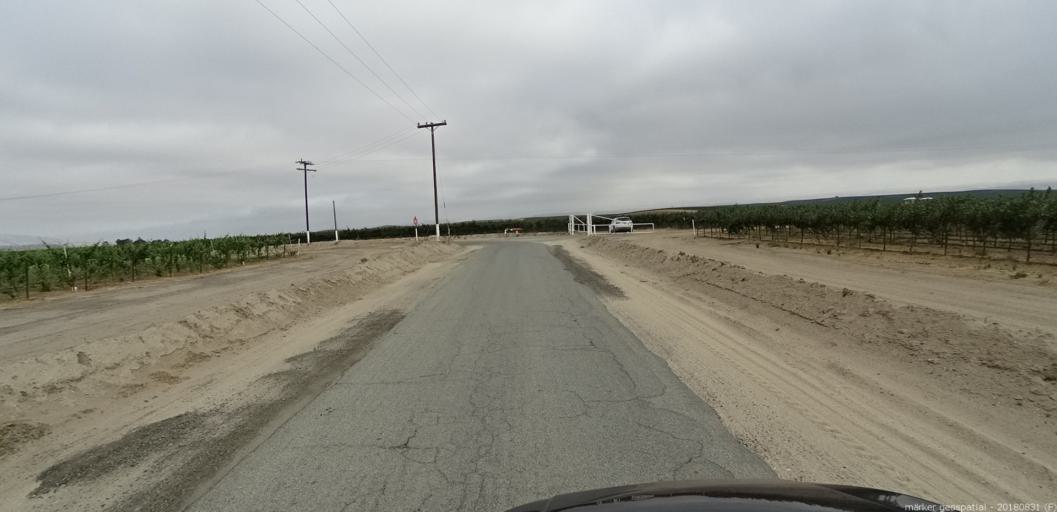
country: US
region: California
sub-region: Monterey County
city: King City
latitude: 36.1393
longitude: -121.0923
